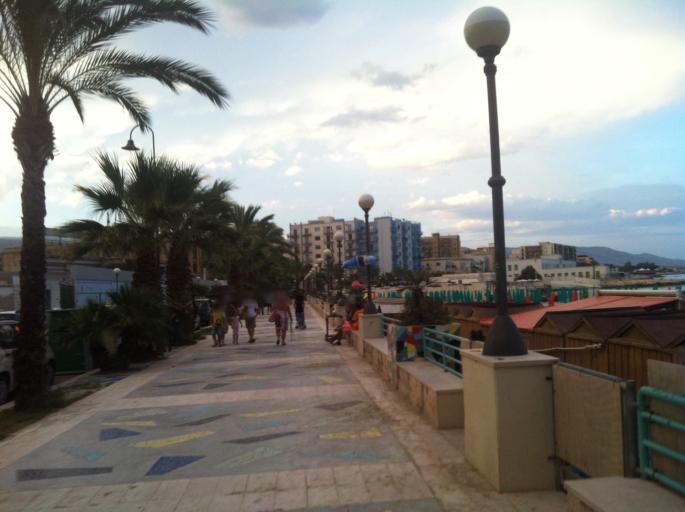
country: IT
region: Apulia
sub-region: Provincia di Foggia
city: Manfredonia
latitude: 41.6310
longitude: 15.9237
